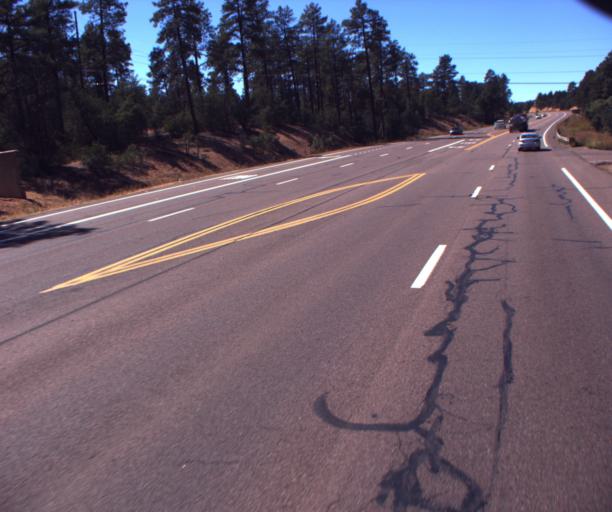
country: US
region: Arizona
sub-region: Gila County
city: Sun Valley
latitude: 34.2523
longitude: -111.2717
